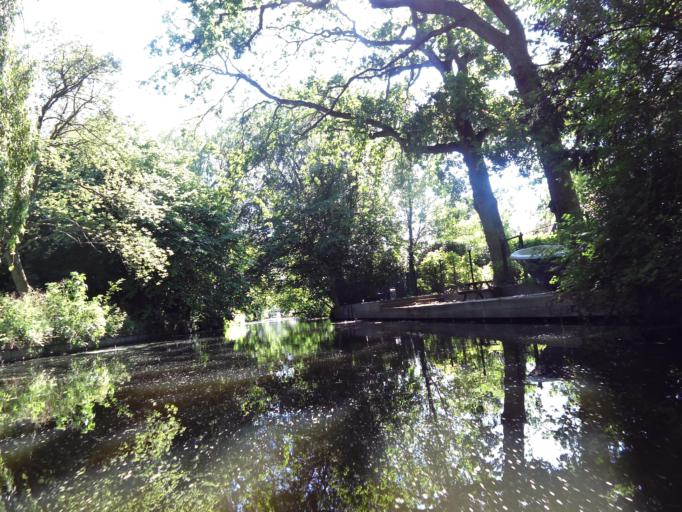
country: NL
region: South Holland
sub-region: Gemeente Wassenaar
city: Wassenaar
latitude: 52.1378
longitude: 4.3958
